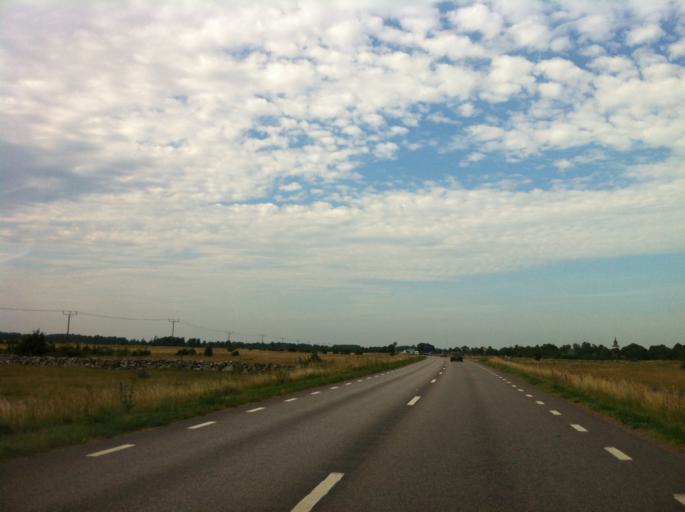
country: SE
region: Kalmar
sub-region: Borgholms Kommun
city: Borgholm
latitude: 56.9397
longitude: 16.7756
